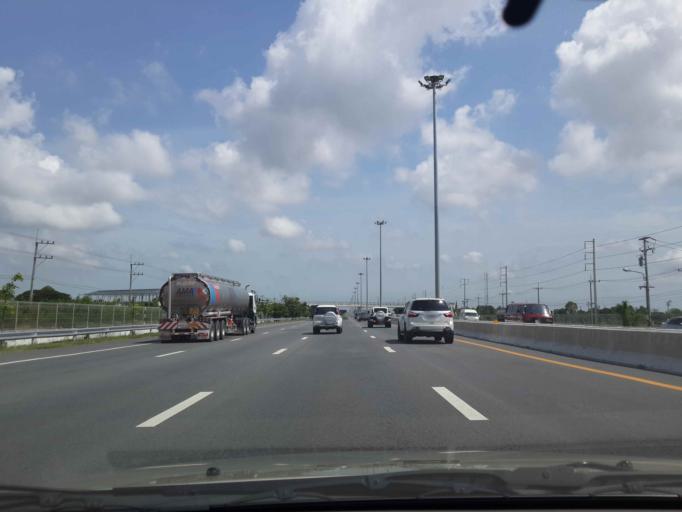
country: TH
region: Chachoengsao
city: Bang Pakong
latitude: 13.5696
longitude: 100.9834
